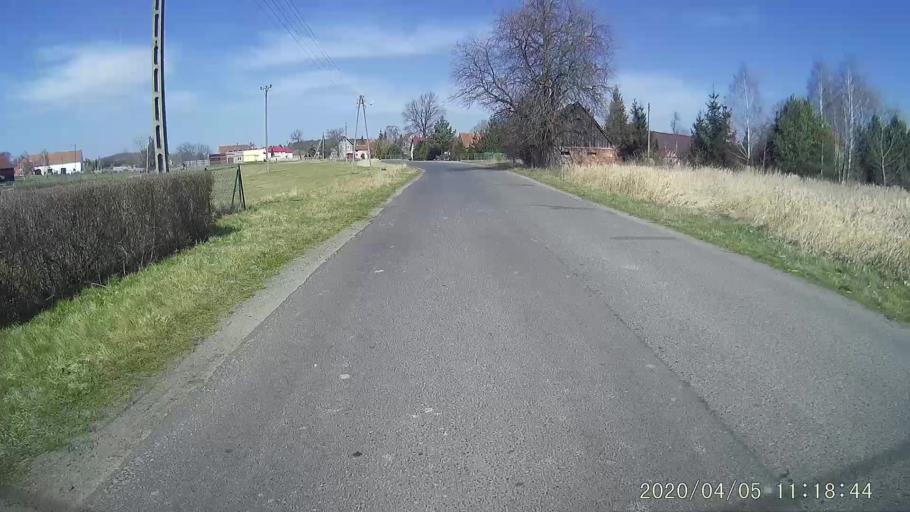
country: PL
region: Lower Silesian Voivodeship
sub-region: Powiat zgorzelecki
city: Sulikow
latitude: 51.0625
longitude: 15.1079
